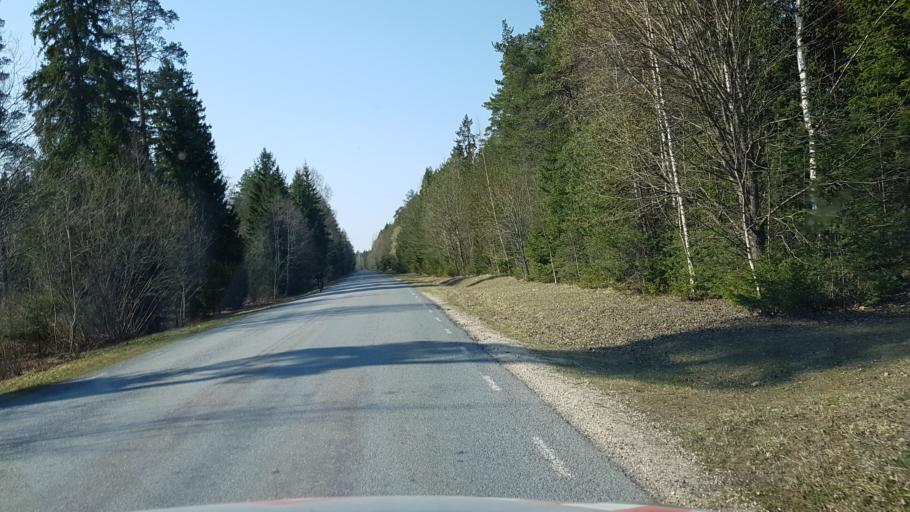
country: EE
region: Raplamaa
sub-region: Maerjamaa vald
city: Marjamaa
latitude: 58.8929
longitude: 24.4022
